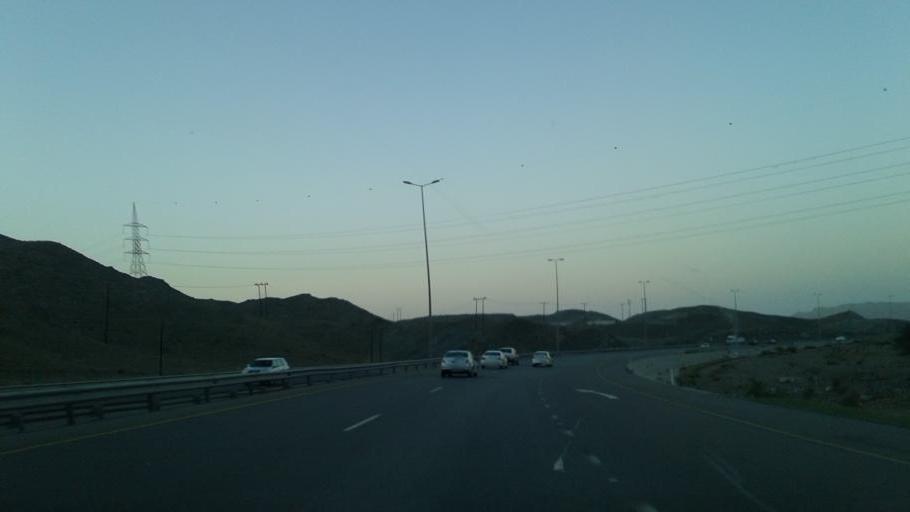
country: OM
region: Muhafazat ad Dakhiliyah
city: Bidbid
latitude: 23.4759
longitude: 58.1958
